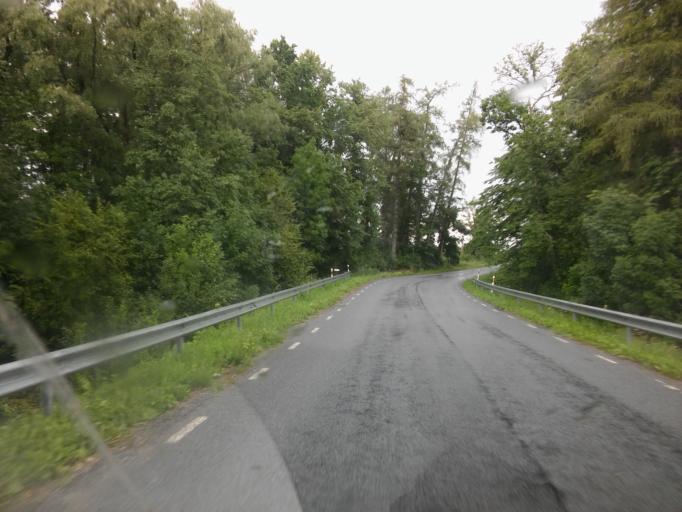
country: EE
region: Raplamaa
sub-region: Maerjamaa vald
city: Marjamaa
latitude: 58.7739
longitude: 24.4675
